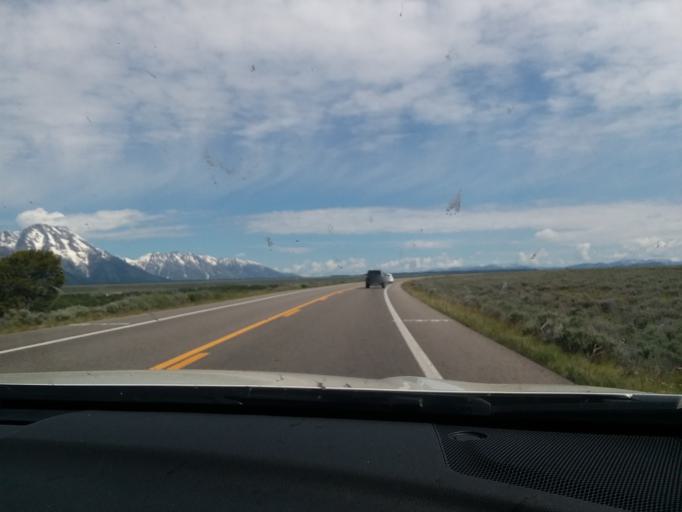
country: US
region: Wyoming
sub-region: Teton County
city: Jackson
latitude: 43.6922
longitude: -110.6723
